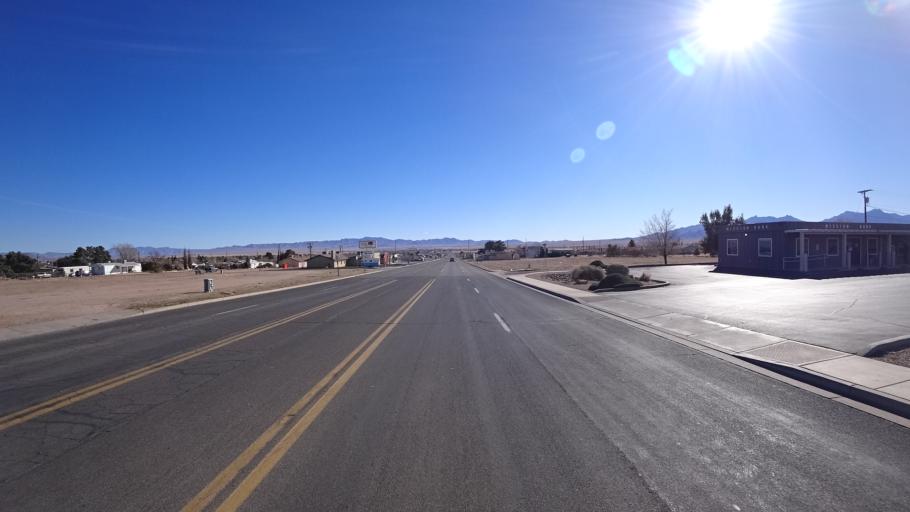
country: US
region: Arizona
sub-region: Mohave County
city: New Kingman-Butler
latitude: 35.2539
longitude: -114.0372
